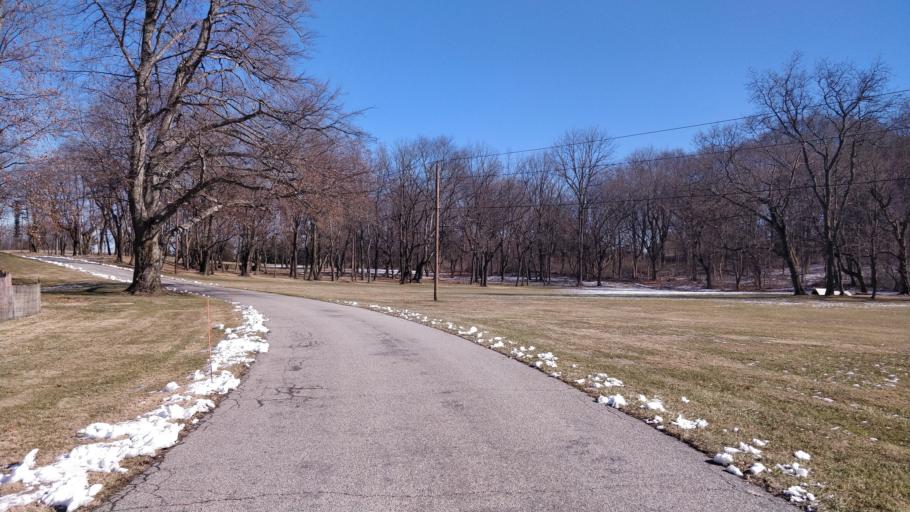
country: US
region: New York
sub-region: Nassau County
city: Old Westbury
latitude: 40.7861
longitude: -73.5858
